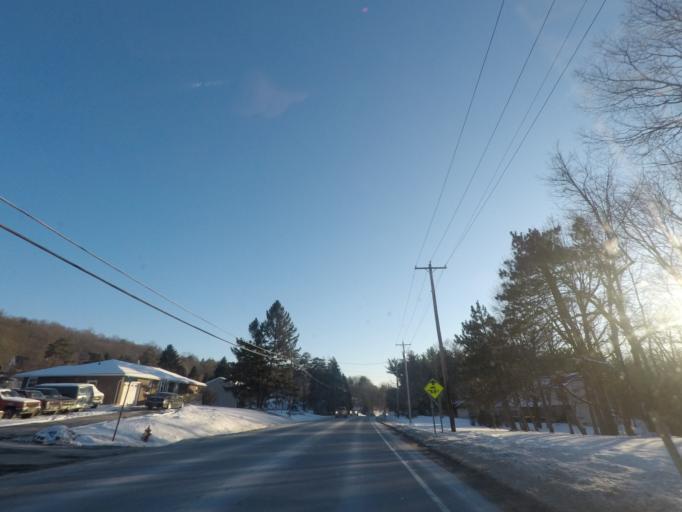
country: US
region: New York
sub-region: Saratoga County
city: Waterford
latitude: 42.8214
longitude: -73.6309
